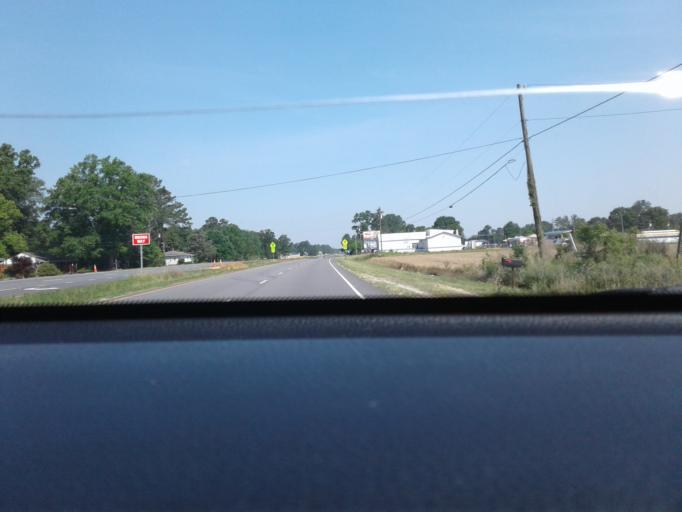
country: US
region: North Carolina
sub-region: Harnett County
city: Erwin
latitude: 35.3556
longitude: -78.6959
